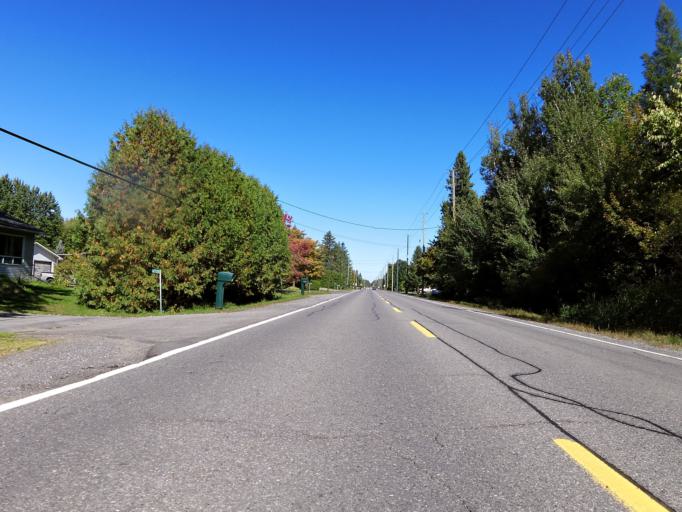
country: CA
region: Ontario
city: Clarence-Rockland
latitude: 45.3622
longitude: -75.4524
